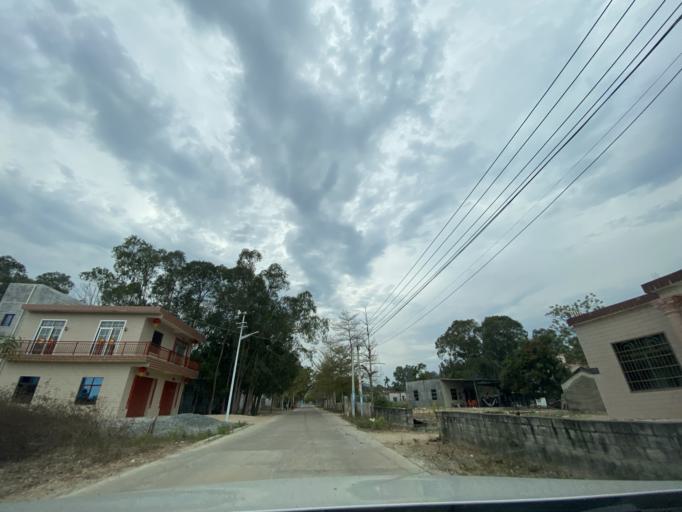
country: CN
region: Hainan
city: Yingzhou
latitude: 18.4202
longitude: 109.8222
